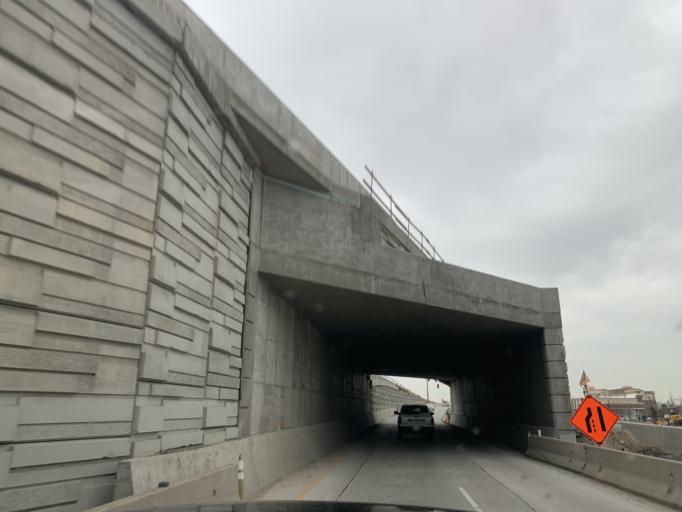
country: US
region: Utah
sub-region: Utah County
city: Lehi
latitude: 40.4297
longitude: -111.8902
